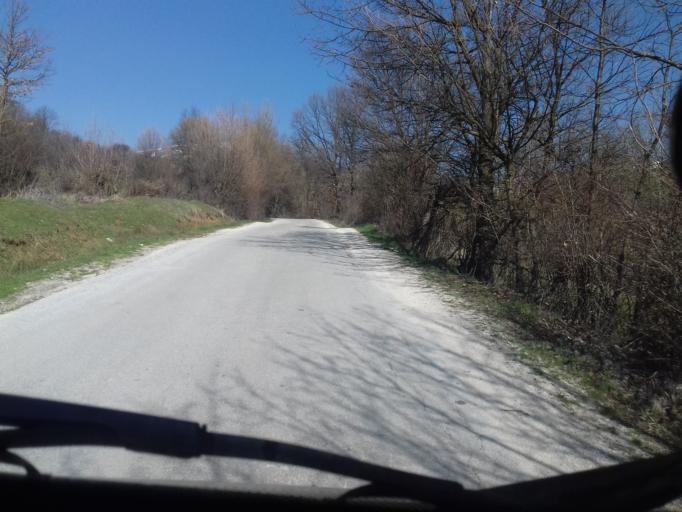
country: BA
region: Federation of Bosnia and Herzegovina
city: Travnik
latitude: 44.2526
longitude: 17.7417
